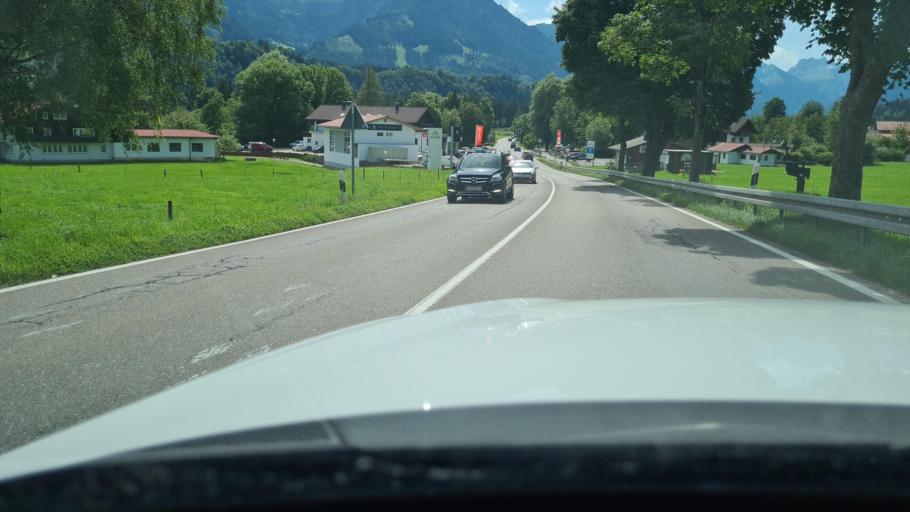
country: DE
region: Bavaria
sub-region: Swabia
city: Obermaiselstein
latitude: 47.4579
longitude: 10.2679
